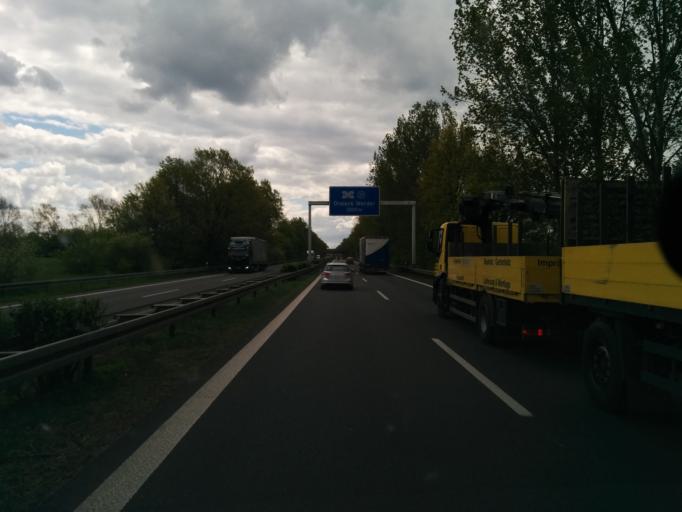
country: DE
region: Brandenburg
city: Gross Kreutz
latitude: 52.3656
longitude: 12.8155
